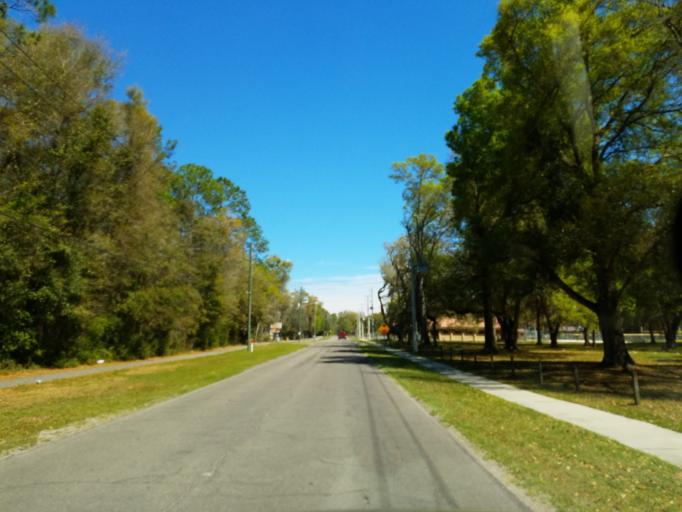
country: US
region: Florida
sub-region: Sumter County
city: Bushnell
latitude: 28.6686
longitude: -82.1073
